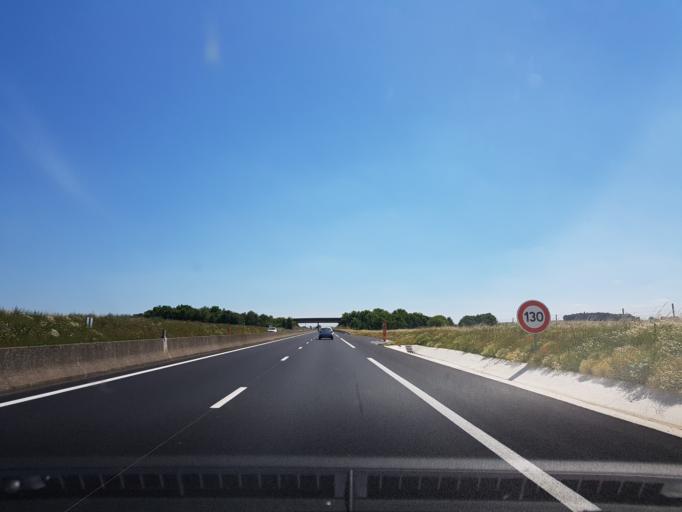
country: FR
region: Picardie
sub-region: Departement de la Somme
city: Nesle
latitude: 49.8355
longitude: 2.9416
